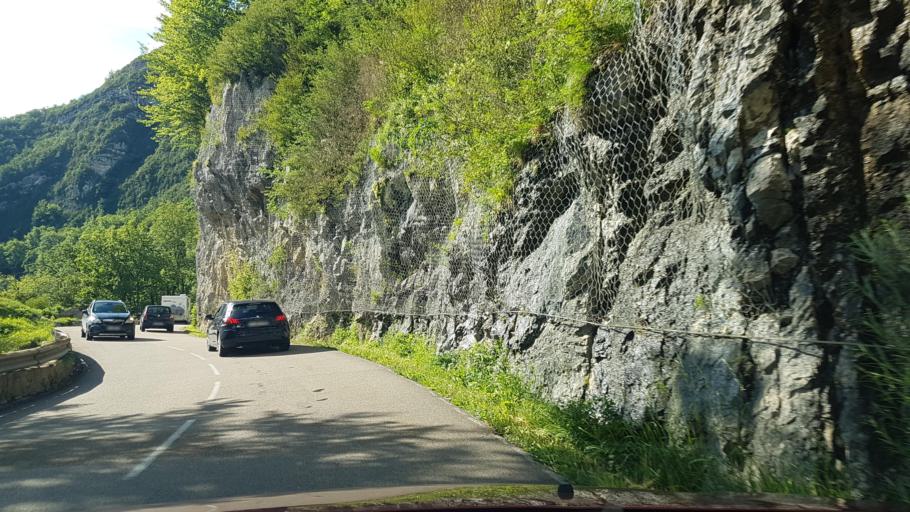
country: FR
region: Franche-Comte
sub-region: Departement du Jura
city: Saint-Claude
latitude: 46.3608
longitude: 5.8966
